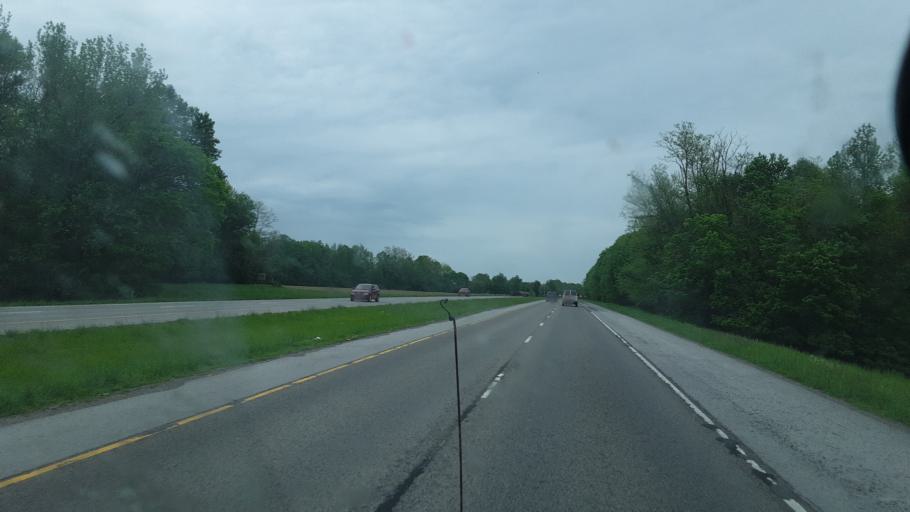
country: US
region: Illinois
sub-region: Jackson County
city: Murphysboro
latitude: 37.7657
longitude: -89.3072
